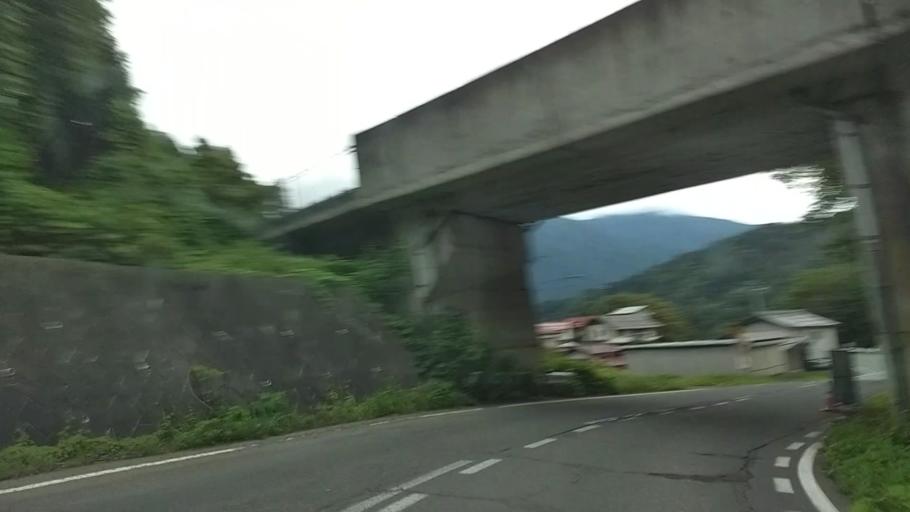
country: JP
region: Nagano
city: Nakano
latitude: 36.7890
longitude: 138.3339
